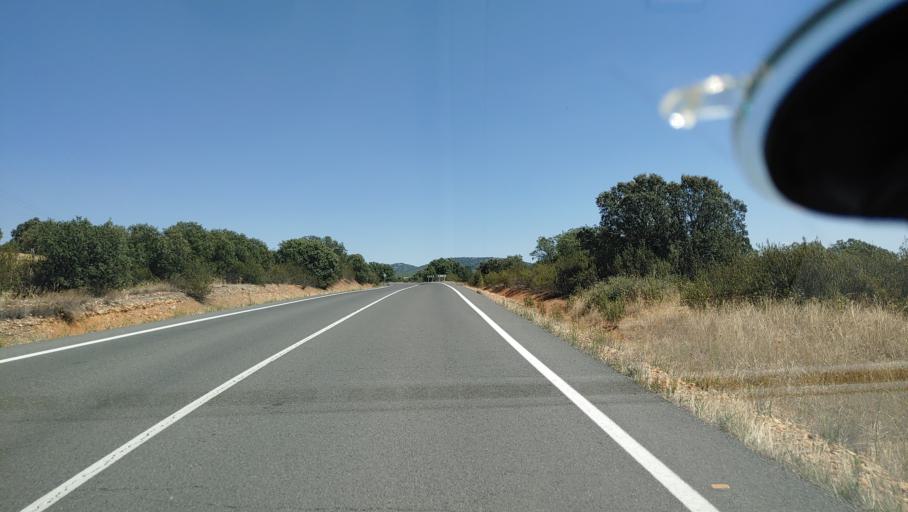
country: ES
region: Castille-La Mancha
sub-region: Provincia de Ciudad Real
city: Almaden
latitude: 38.8325
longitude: -4.7017
